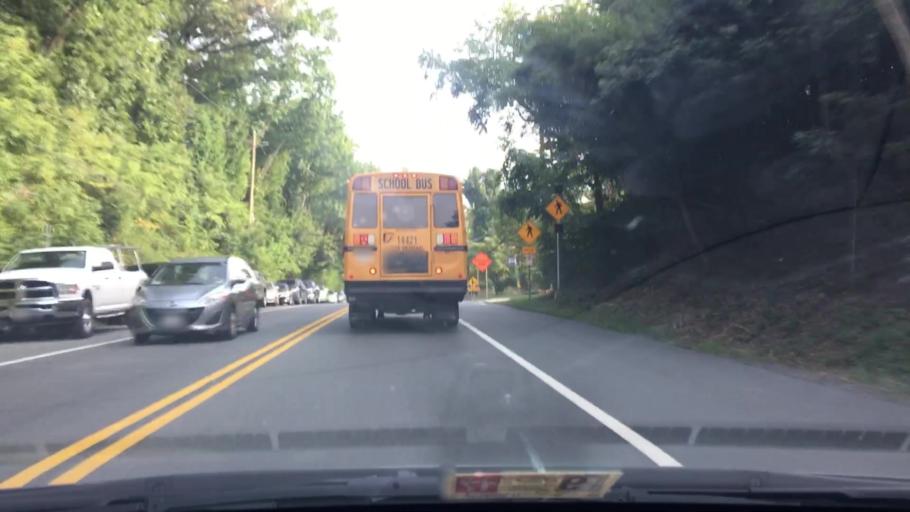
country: US
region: Maryland
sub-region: Montgomery County
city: North Bethesda
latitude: 39.0299
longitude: -77.1617
